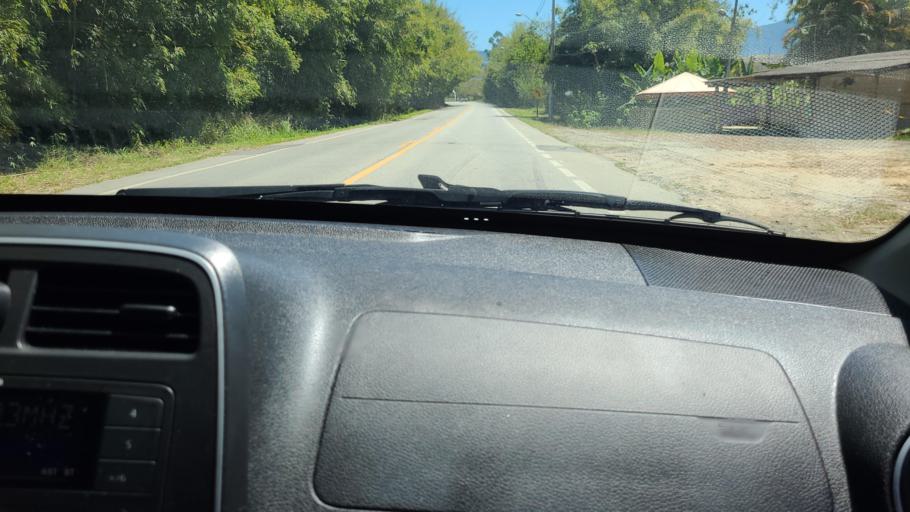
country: BR
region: Sao Paulo
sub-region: Pindamonhangaba
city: Pindamonhangaba
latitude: -22.8863
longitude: -45.5137
